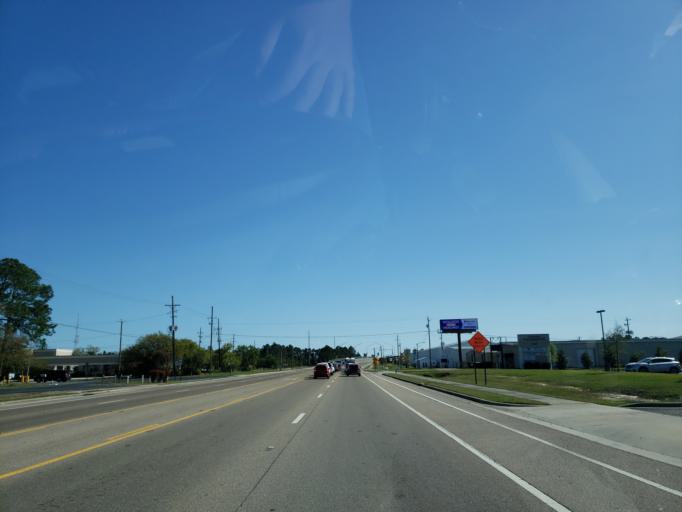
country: US
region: Mississippi
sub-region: Harrison County
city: West Gulfport
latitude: 30.4298
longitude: -89.0312
